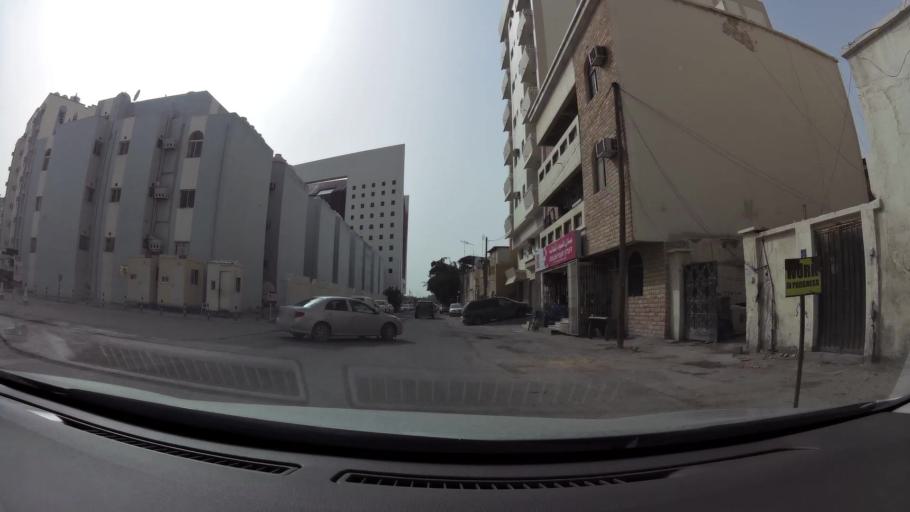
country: QA
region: Baladiyat ad Dawhah
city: Doha
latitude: 25.2756
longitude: 51.5505
